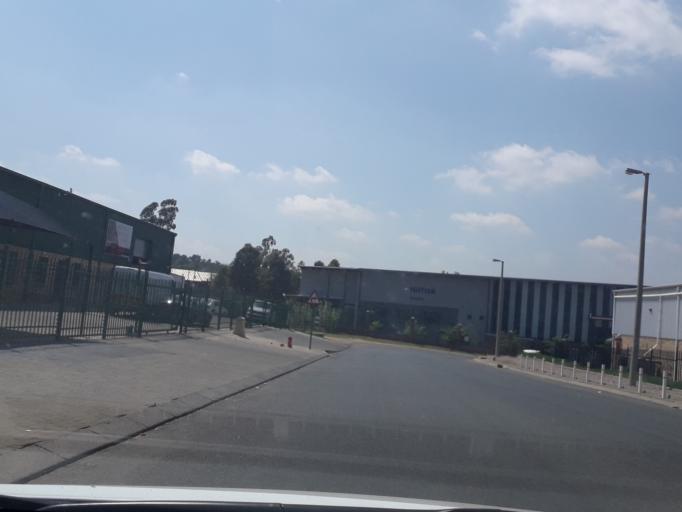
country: ZA
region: Gauteng
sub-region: West Rand District Municipality
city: Muldersdriseloop
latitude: -26.0756
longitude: 27.9129
